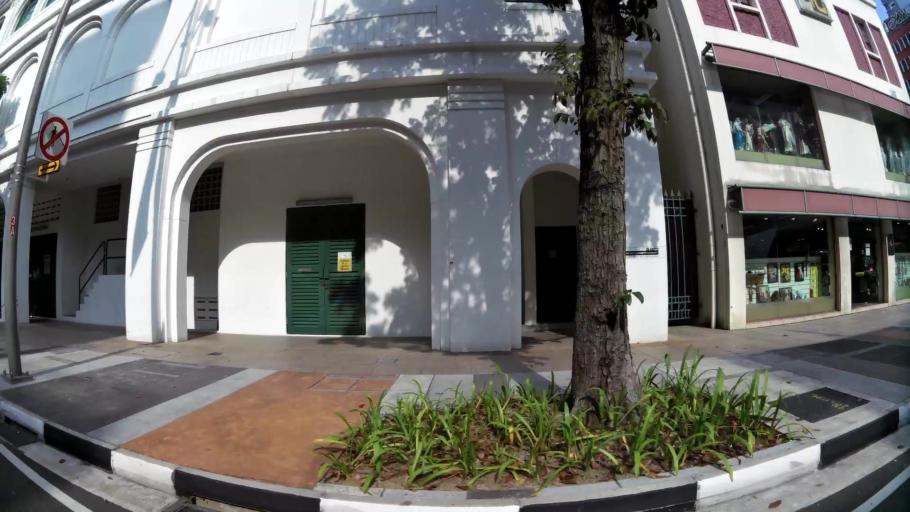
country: SG
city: Singapore
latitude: 1.2973
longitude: 103.8516
